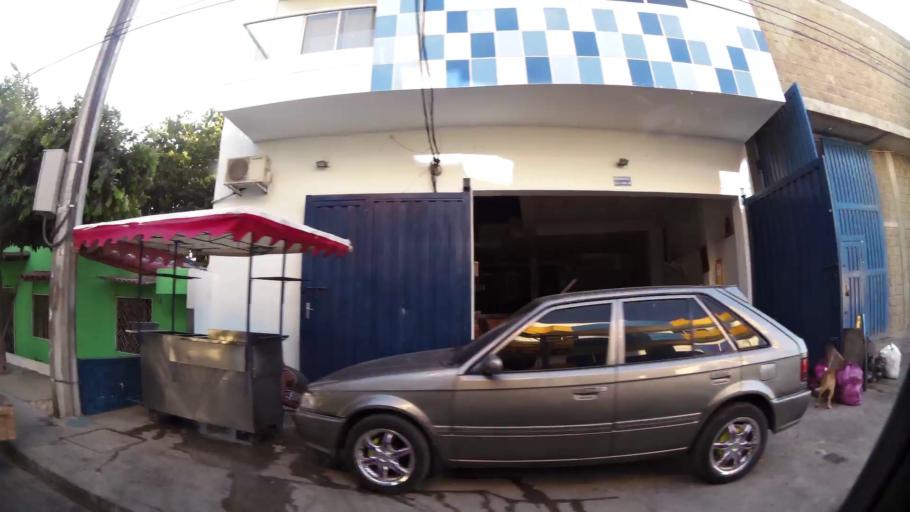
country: CO
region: Bolivar
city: Cartagena
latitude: 10.4006
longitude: -75.5205
